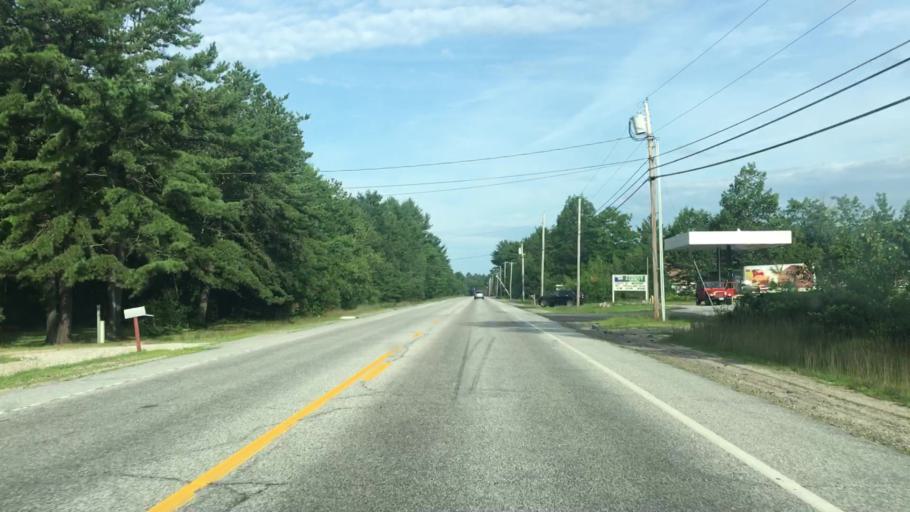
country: US
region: Maine
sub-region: Cumberland County
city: Steep Falls
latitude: 43.7338
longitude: -70.6177
